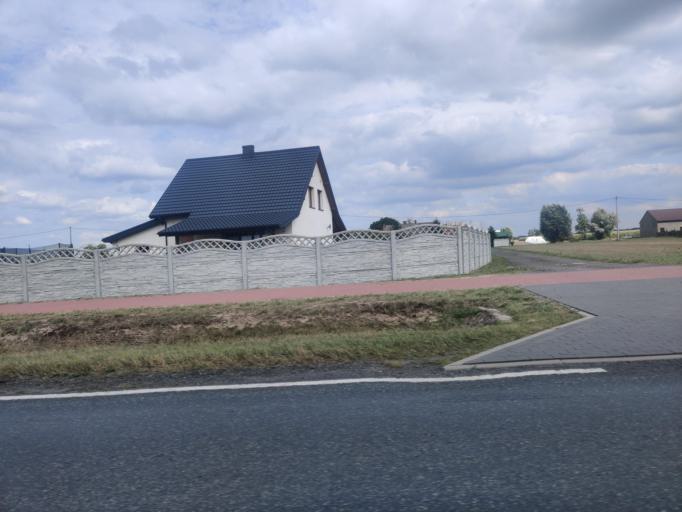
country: PL
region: Greater Poland Voivodeship
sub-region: Powiat koninski
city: Rychwal
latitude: 52.1126
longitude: 18.1676
